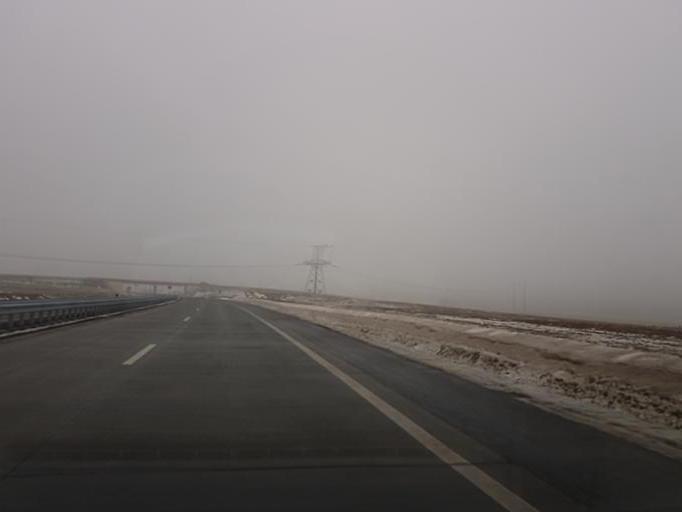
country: BY
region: Minsk
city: Atolina
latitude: 53.7613
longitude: 27.3982
